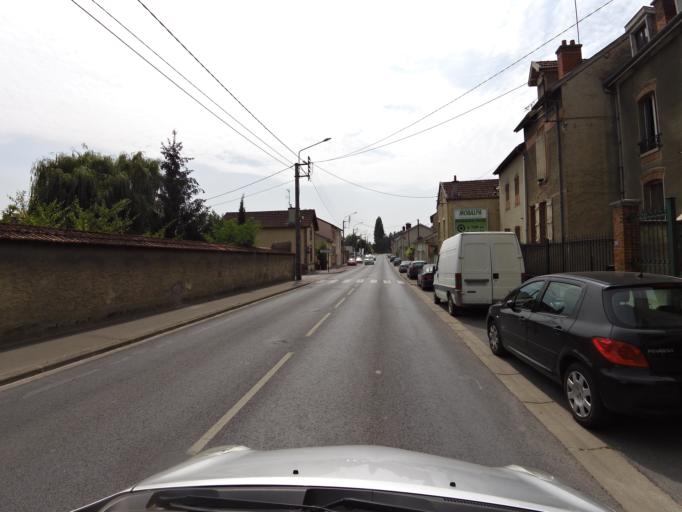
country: FR
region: Champagne-Ardenne
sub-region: Departement de la Marne
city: Pierry
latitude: 49.0340
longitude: 3.9481
